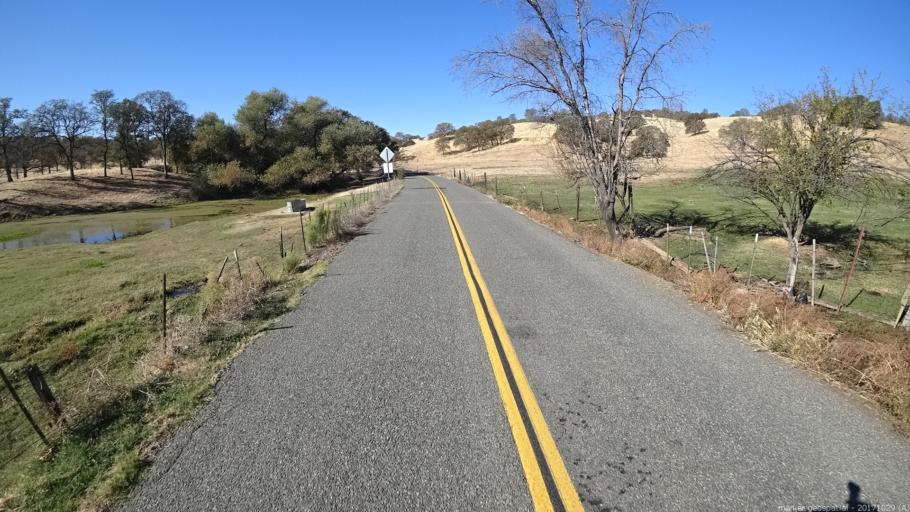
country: US
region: California
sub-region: Shasta County
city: Shasta
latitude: 40.4507
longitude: -122.6360
